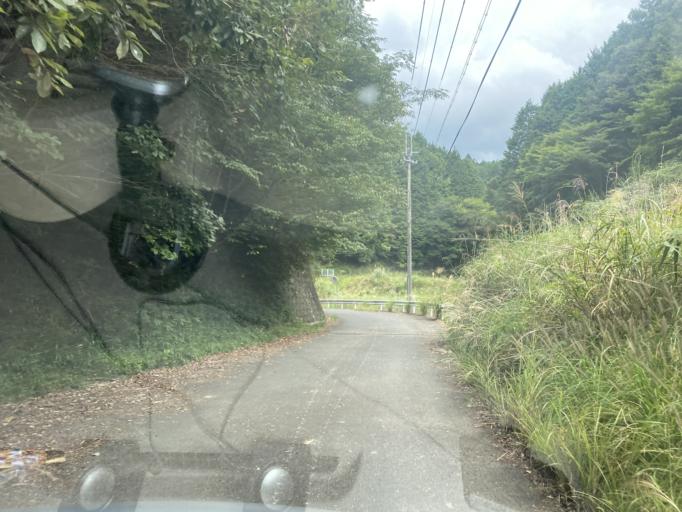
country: JP
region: Nara
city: Nara-shi
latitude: 34.6761
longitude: 135.8907
